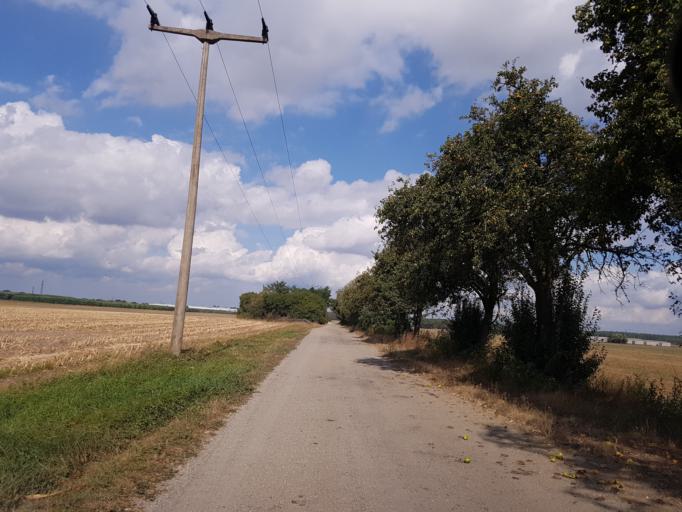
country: DE
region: Brandenburg
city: Finsterwalde
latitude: 51.6233
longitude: 13.7566
